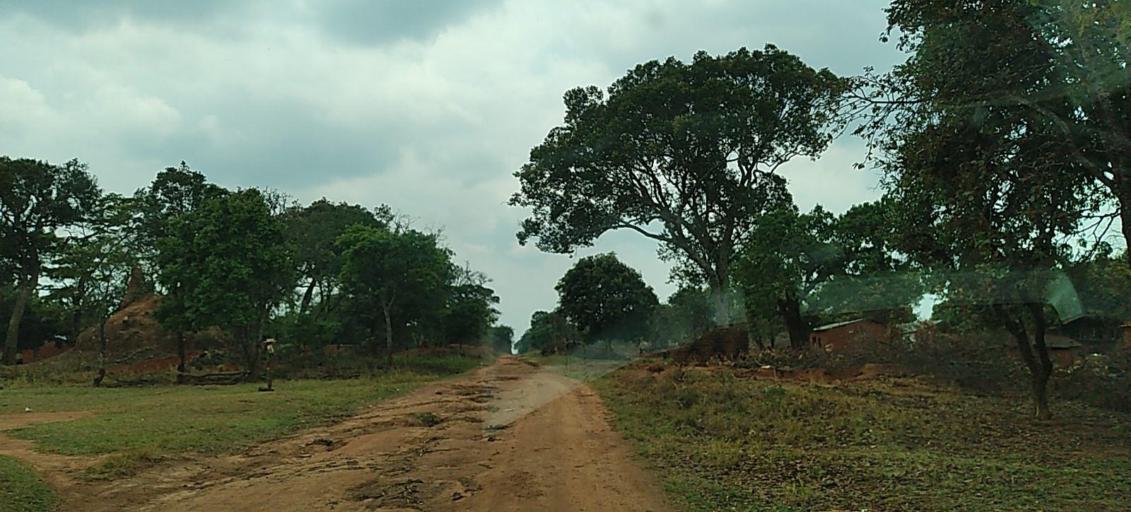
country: ZM
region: North-Western
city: Mwinilunga
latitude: -11.5318
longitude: 24.7847
